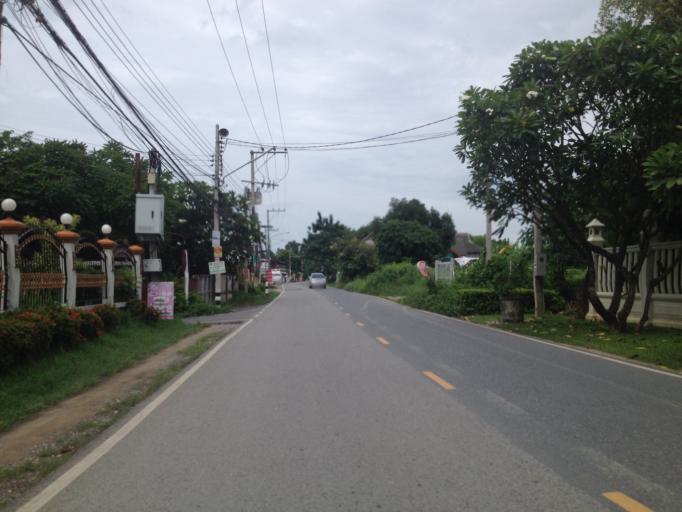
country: TH
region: Chiang Mai
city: Saraphi
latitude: 18.7144
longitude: 98.9849
